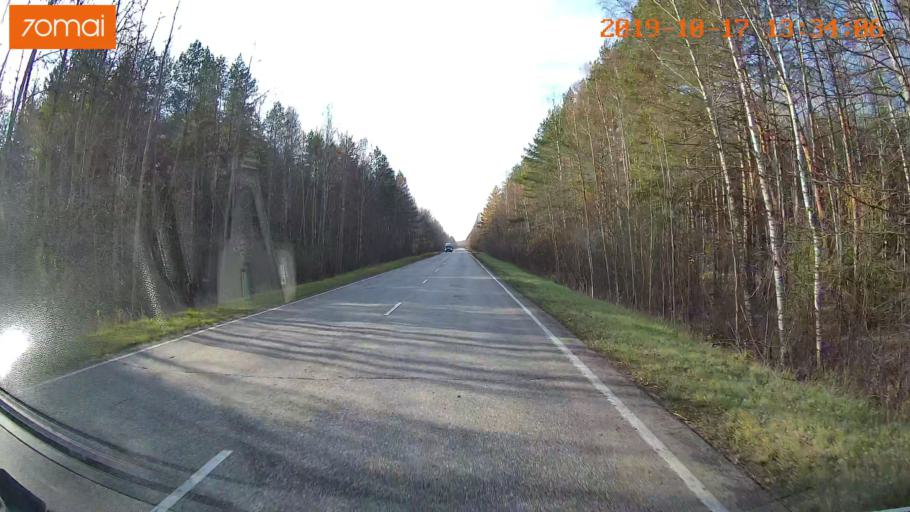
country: RU
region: Vladimir
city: Velikodvorskiy
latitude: 55.1445
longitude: 40.7248
